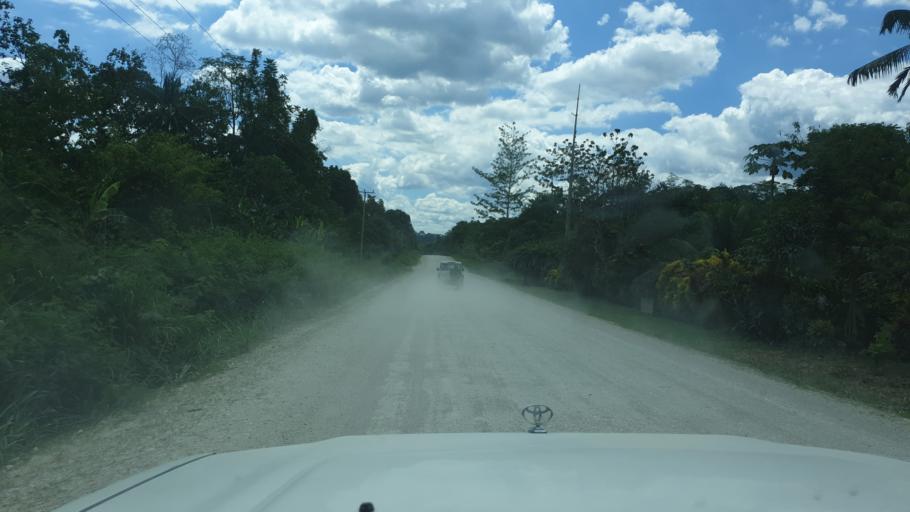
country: PG
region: Madang
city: Madang
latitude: -5.5600
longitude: 145.4159
